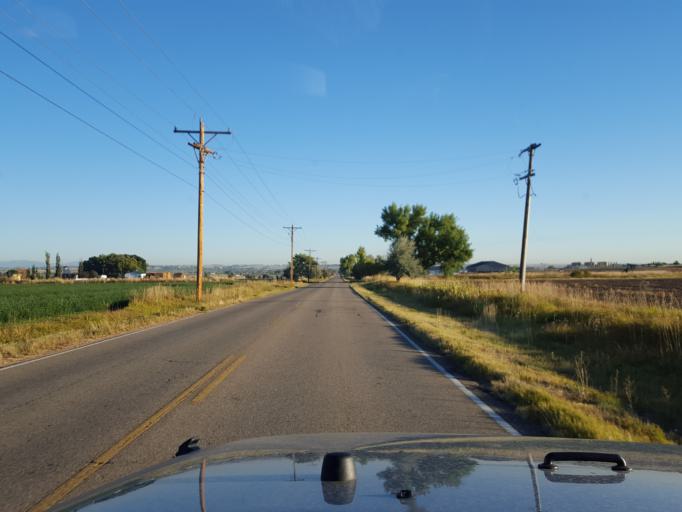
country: US
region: Colorado
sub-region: Weld County
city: Firestone
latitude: 40.1115
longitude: -104.9988
